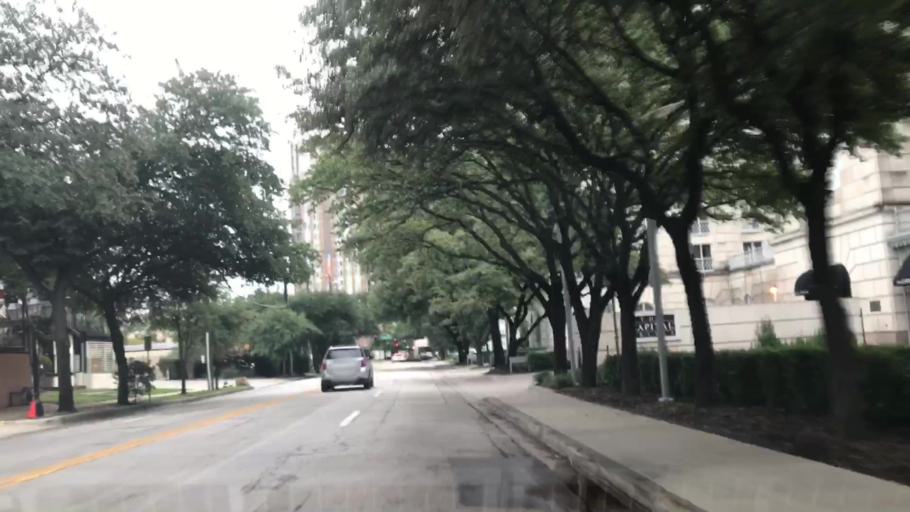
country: US
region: Texas
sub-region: Dallas County
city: Dallas
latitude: 32.7951
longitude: -96.8041
